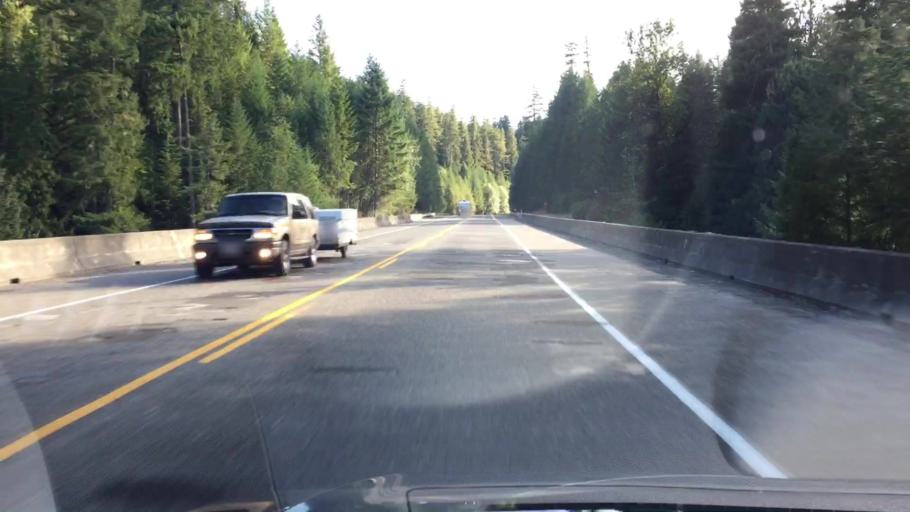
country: US
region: Washington
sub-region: Pierce County
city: Buckley
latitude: 46.6791
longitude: -121.5755
